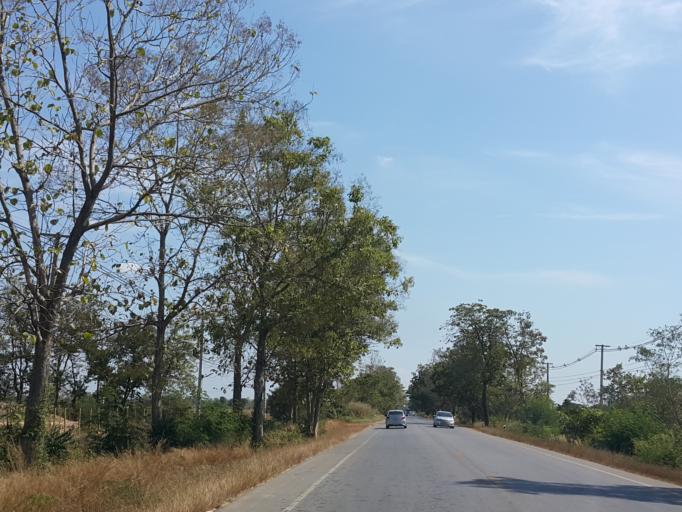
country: TH
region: Sukhothai
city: Sawankhalok
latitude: 17.3098
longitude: 99.7195
